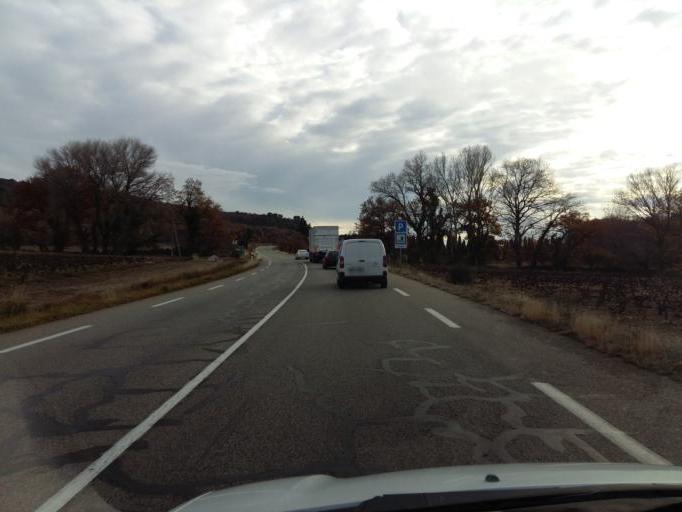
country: FR
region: Provence-Alpes-Cote d'Azur
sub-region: Departement du Vaucluse
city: Visan
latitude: 44.3361
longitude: 4.9472
